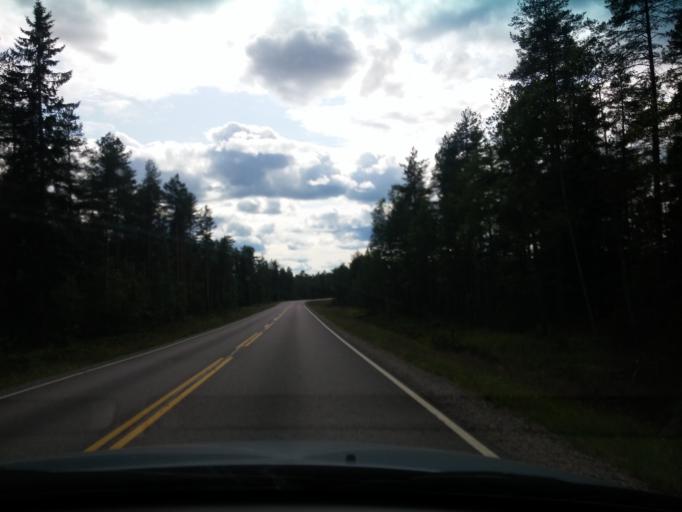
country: FI
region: Central Finland
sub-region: Saarijaervi-Viitasaari
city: Pylkoenmaeki
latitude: 62.6233
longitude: 24.7798
